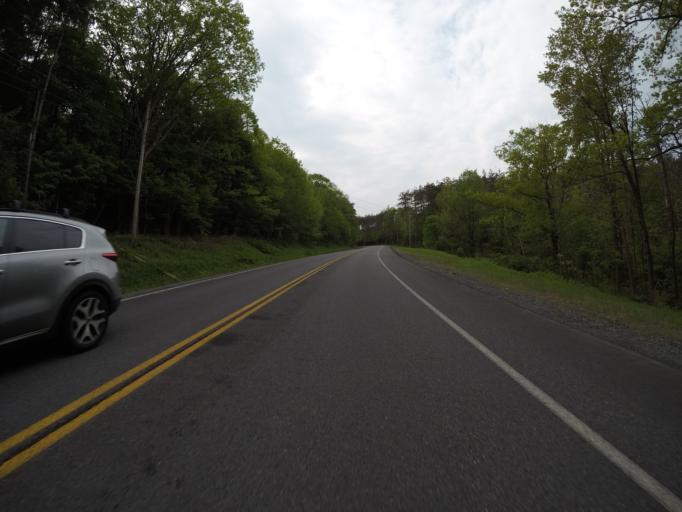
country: US
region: New York
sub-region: Sullivan County
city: Livingston Manor
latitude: 42.0419
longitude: -74.9041
